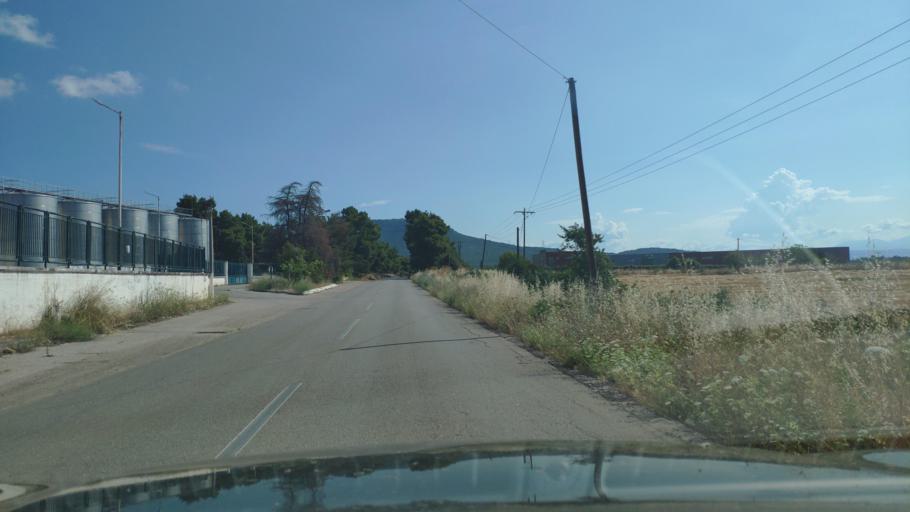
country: GR
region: Central Greece
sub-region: Nomos Voiotias
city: Arma
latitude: 38.3971
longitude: 23.5123
